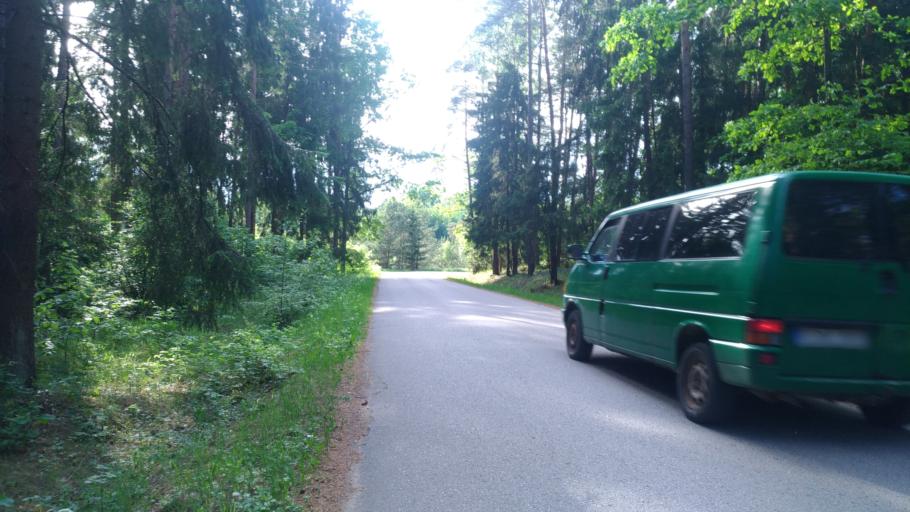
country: LT
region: Kauno apskritis
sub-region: Kauno rajonas
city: Karmelava
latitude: 54.9891
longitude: 24.1134
